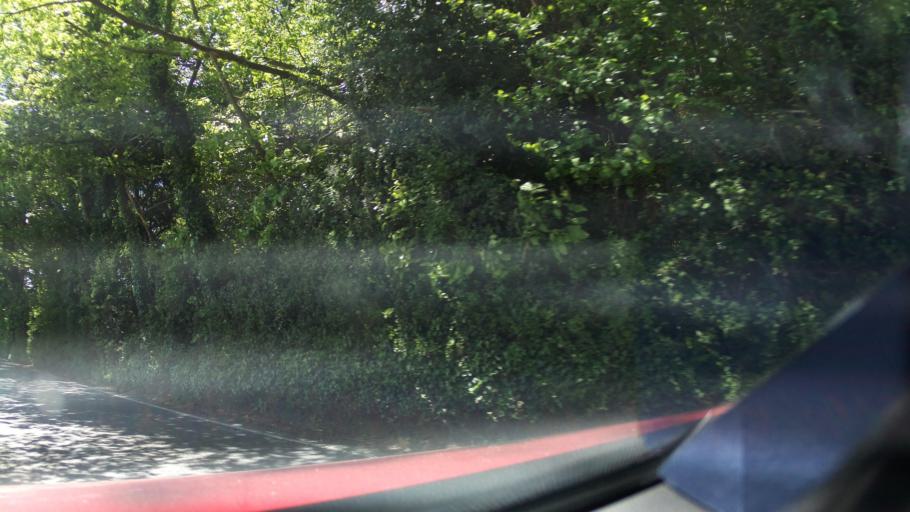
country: GB
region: England
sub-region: Devon
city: Newton Poppleford
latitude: 50.6911
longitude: -3.3045
